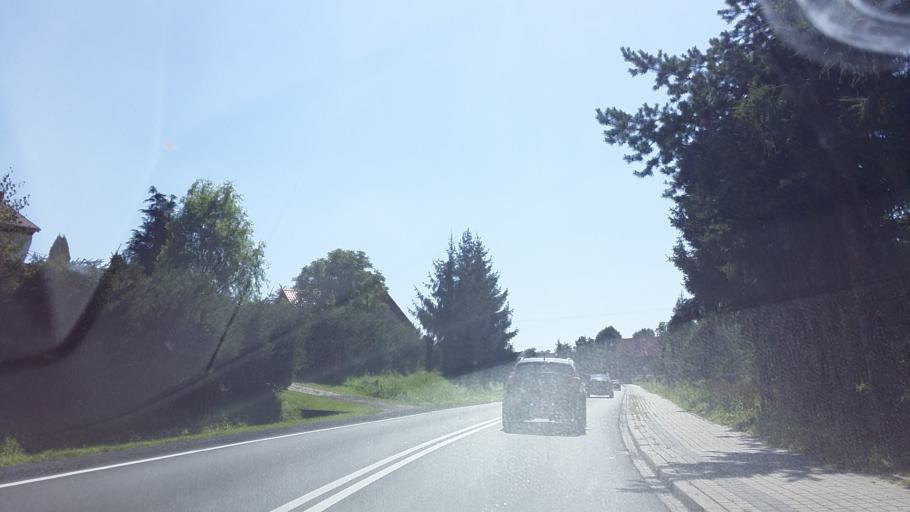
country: PL
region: Lesser Poland Voivodeship
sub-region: Powiat wadowicki
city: Radocza
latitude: 49.9464
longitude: 19.4491
